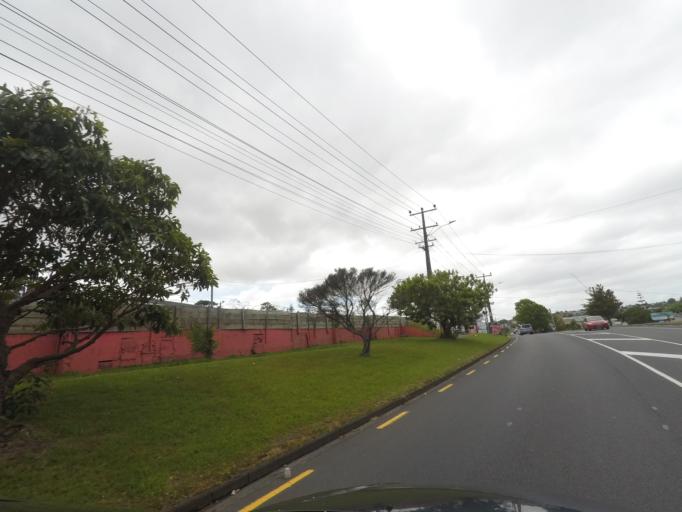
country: NZ
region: Auckland
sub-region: Auckland
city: Waitakere
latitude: -36.9088
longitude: 174.6473
